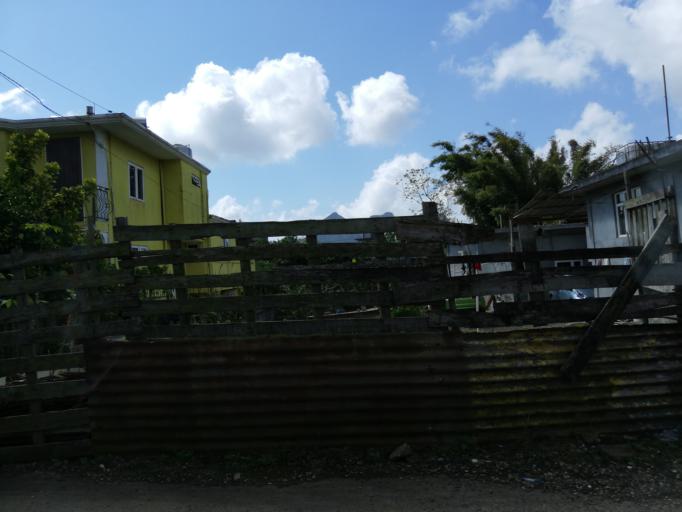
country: MU
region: Moka
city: Verdun
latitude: -20.2245
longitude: 57.5416
